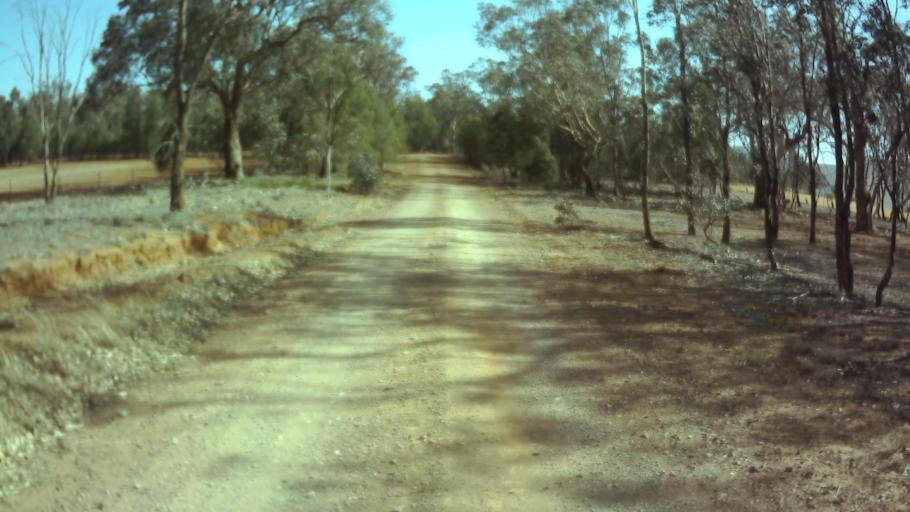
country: AU
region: New South Wales
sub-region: Weddin
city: Grenfell
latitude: -33.8599
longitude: 148.0151
